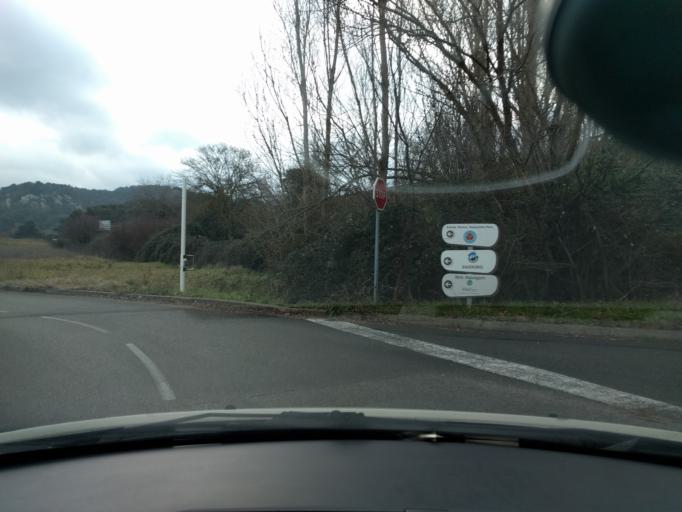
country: FR
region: Provence-Alpes-Cote d'Azur
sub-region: Departement des Bouches-du-Rhone
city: Cabries
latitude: 43.4303
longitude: 5.3971
